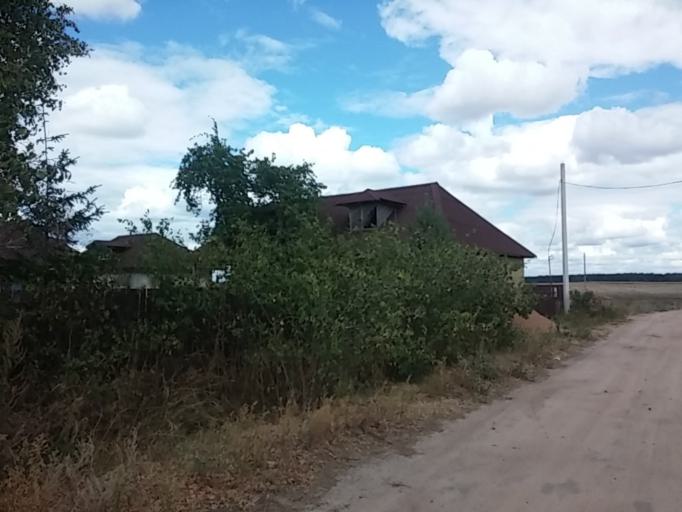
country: BY
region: Minsk
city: Chervyen'
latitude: 53.7816
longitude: 28.2696
